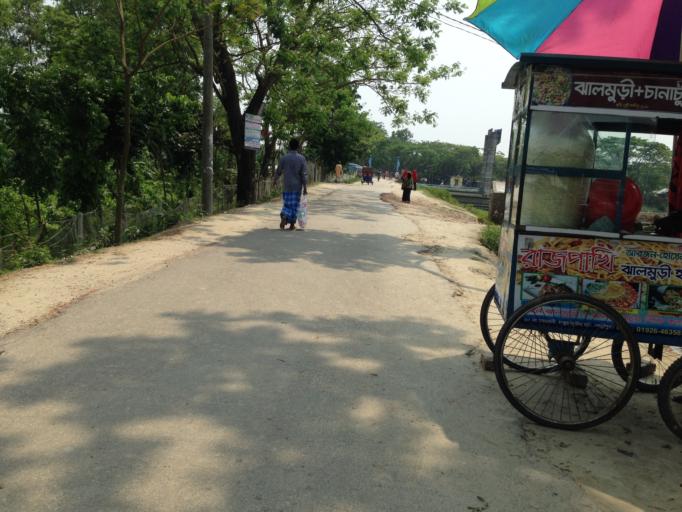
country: BD
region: Chittagong
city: Lakshmipur
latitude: 22.8725
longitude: 90.7844
